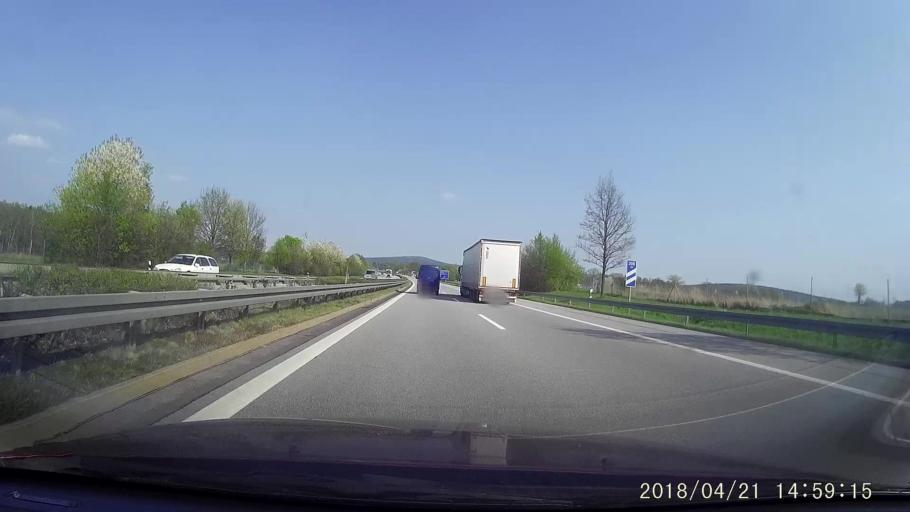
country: DE
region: Saxony
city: Reichenbach
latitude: 51.2037
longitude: 14.7541
